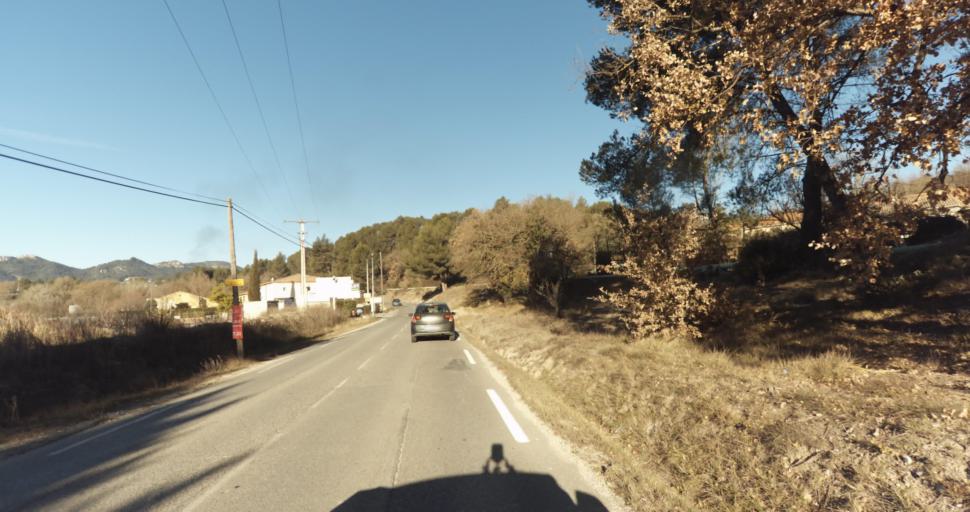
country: FR
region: Provence-Alpes-Cote d'Azur
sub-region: Departement des Bouches-du-Rhone
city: La Bouilladisse
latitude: 43.3956
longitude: 5.5849
